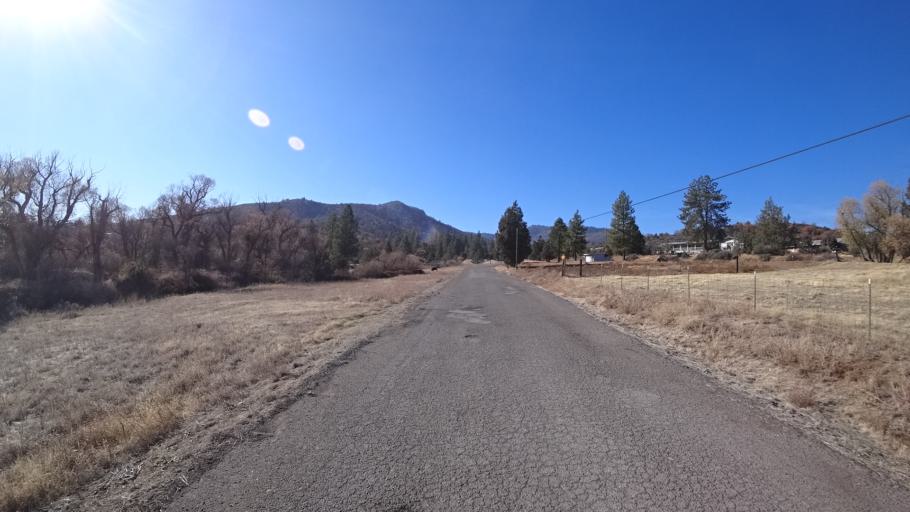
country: US
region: California
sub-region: Siskiyou County
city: Yreka
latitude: 41.7599
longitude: -122.6277
